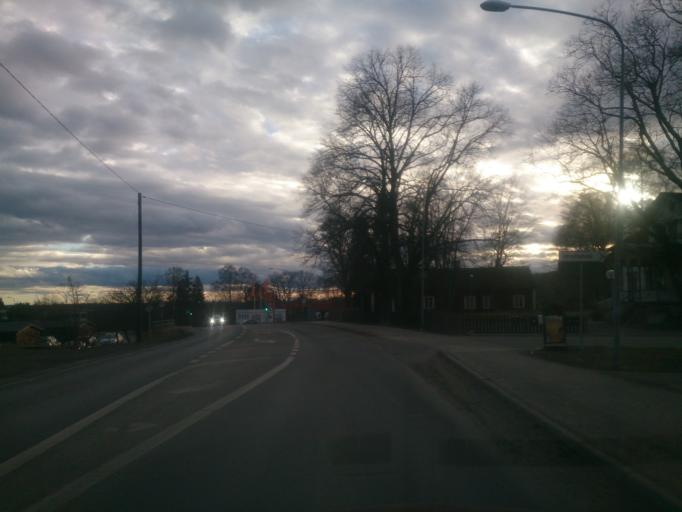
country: SE
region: OEstergoetland
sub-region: Norrkopings Kommun
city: Jursla
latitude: 58.6614
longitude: 16.1767
